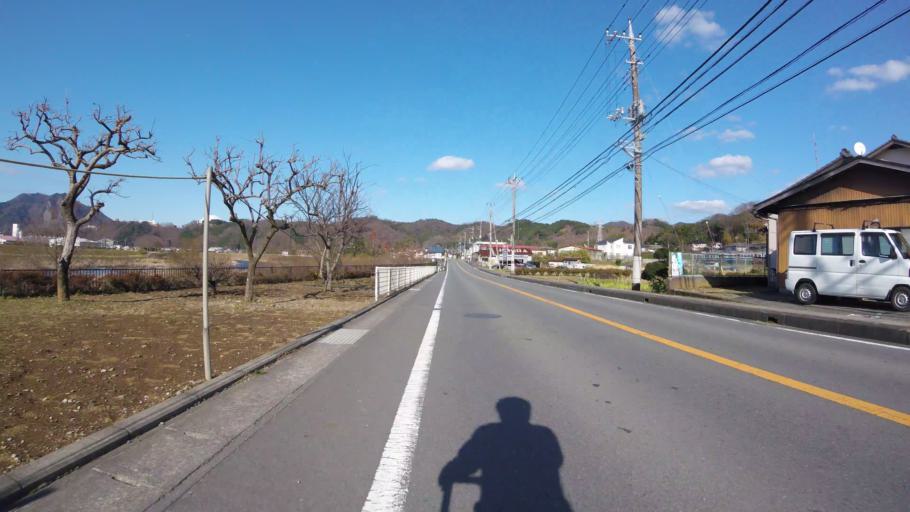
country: JP
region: Shizuoka
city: Ito
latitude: 34.9854
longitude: 138.9532
